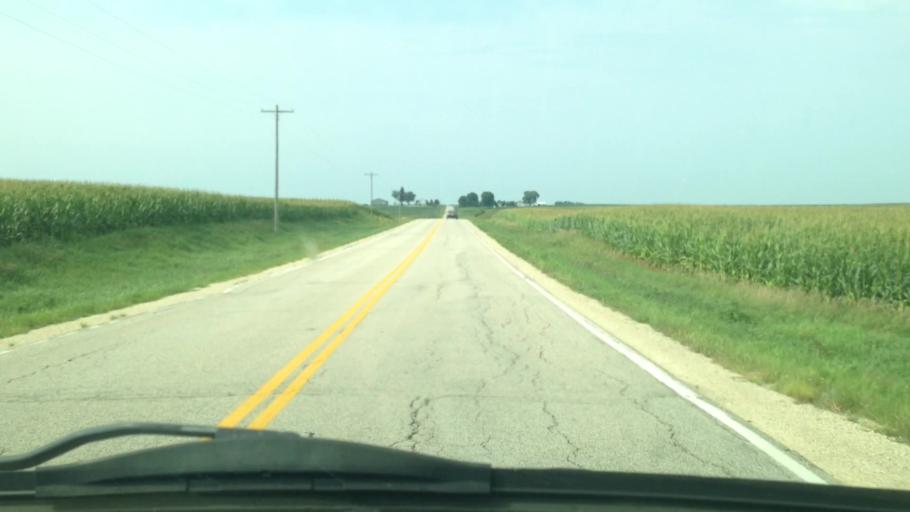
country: US
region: Minnesota
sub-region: Winona County
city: Lewiston
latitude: 43.8832
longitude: -91.9594
